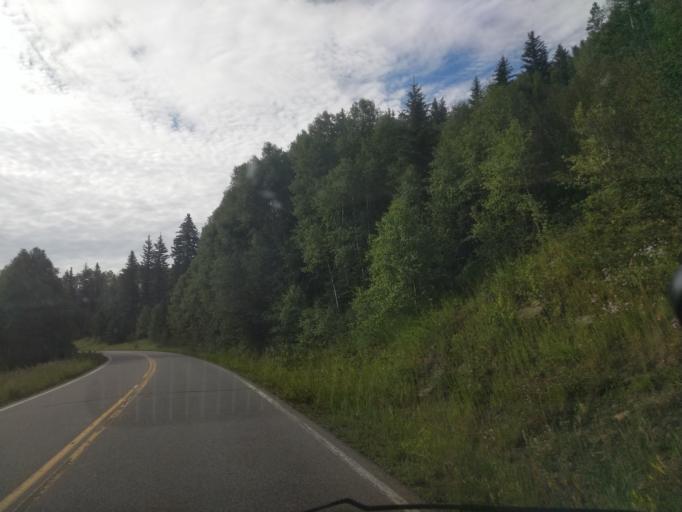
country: US
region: Colorado
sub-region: Garfield County
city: Carbondale
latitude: 39.1004
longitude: -107.2633
